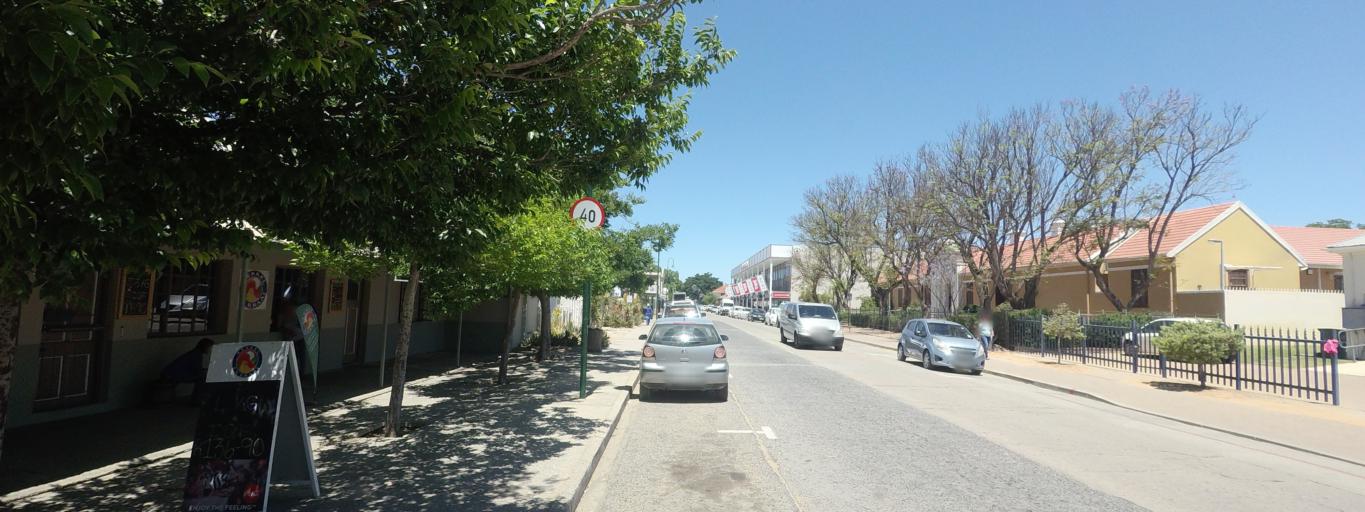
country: ZA
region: Western Cape
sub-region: West Coast District Municipality
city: Clanwilliam
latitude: -32.1764
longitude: 18.8928
